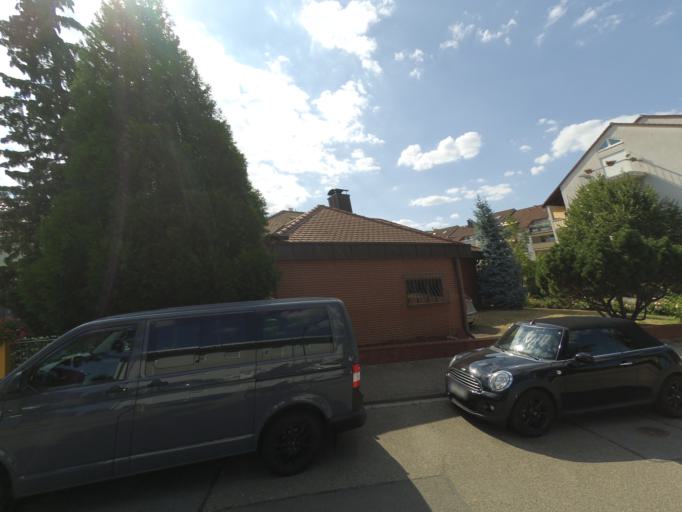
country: DE
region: Rheinland-Pfalz
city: Gartenstadt
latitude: 49.4632
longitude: 8.4124
